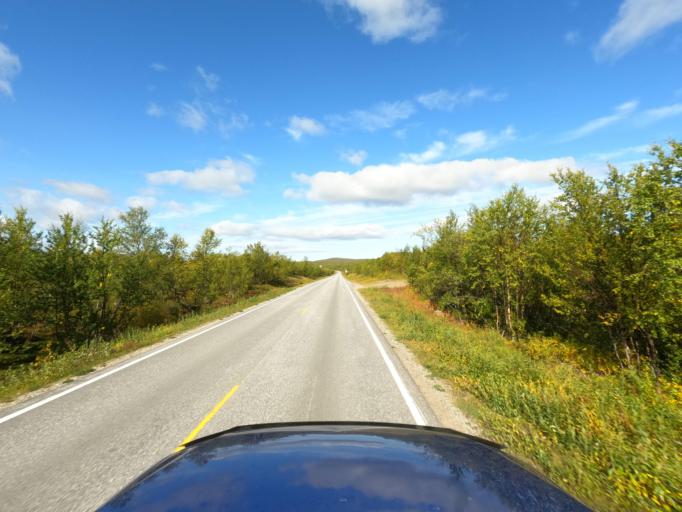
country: NO
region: Finnmark Fylke
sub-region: Karasjok
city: Karasjohka
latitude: 69.5348
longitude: 25.4344
